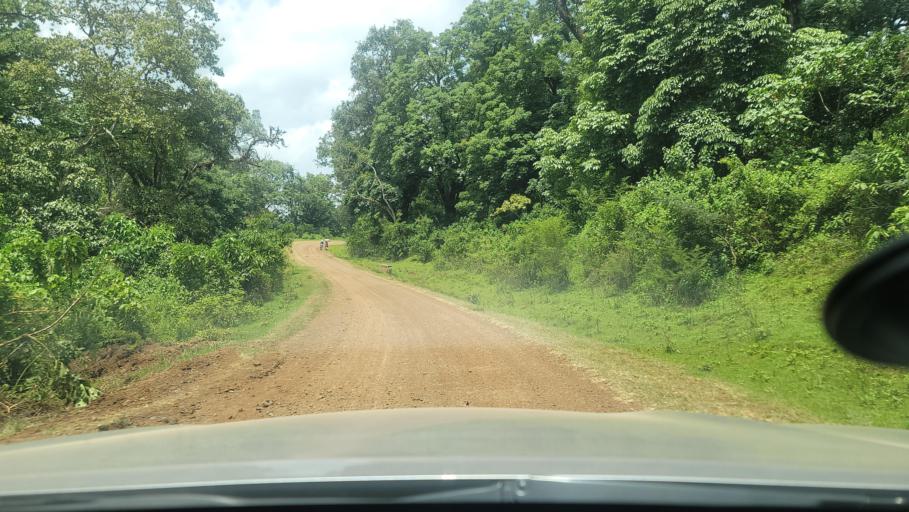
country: ET
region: Oromiya
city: Agaro
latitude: 7.7087
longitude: 36.2531
